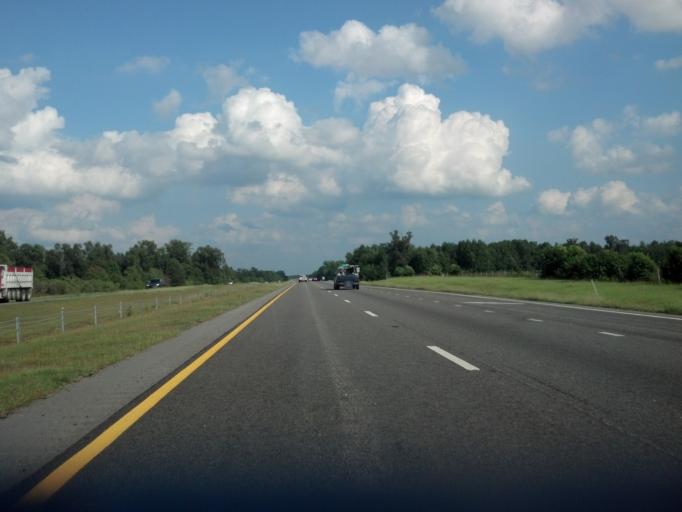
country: US
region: North Carolina
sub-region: Pitt County
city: Bethel
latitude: 35.8410
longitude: -77.4000
